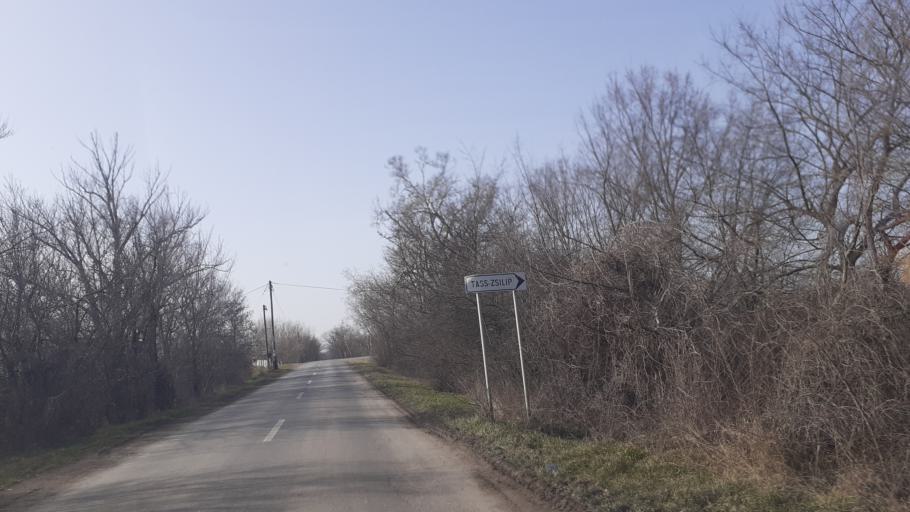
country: HU
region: Fejer
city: Racalmas
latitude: 47.0229
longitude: 18.9839
